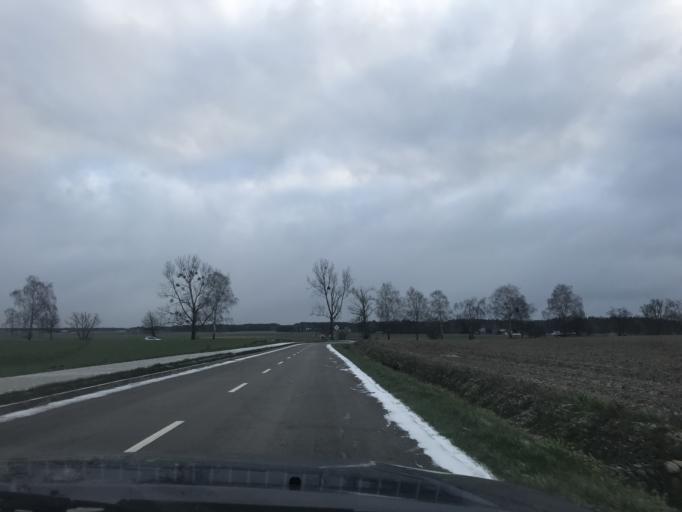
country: PL
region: Pomeranian Voivodeship
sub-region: Powiat chojnicki
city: Brusy
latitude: 53.8702
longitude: 17.7556
